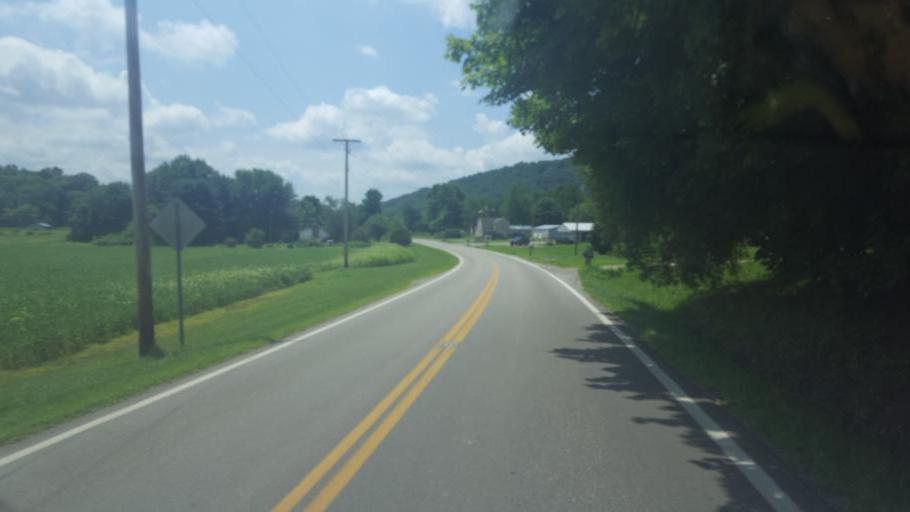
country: US
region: Ohio
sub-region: Ross County
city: Kingston
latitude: 39.3366
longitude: -82.7286
